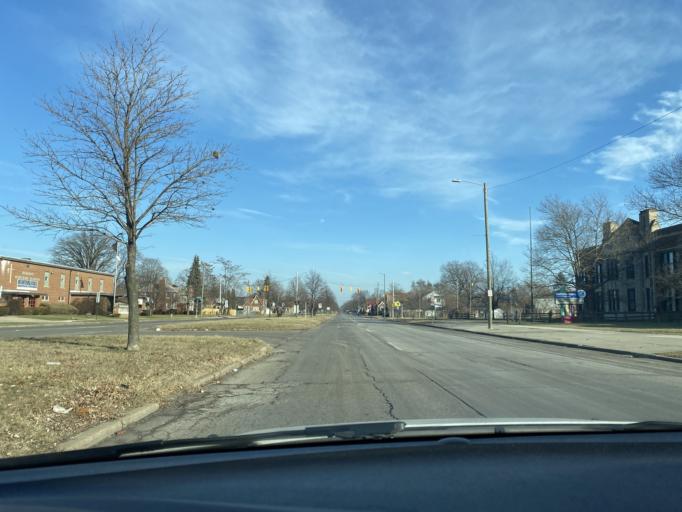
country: US
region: Michigan
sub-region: Wayne County
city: Grosse Pointe Park
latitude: 42.4050
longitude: -82.9492
